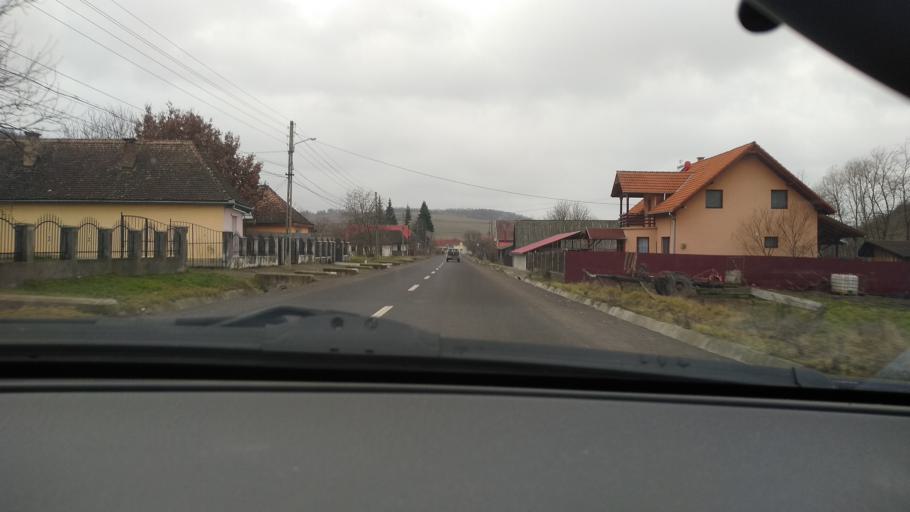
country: RO
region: Mures
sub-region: Comuna Magherani
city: Magherani
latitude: 46.5603
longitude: 24.8984
